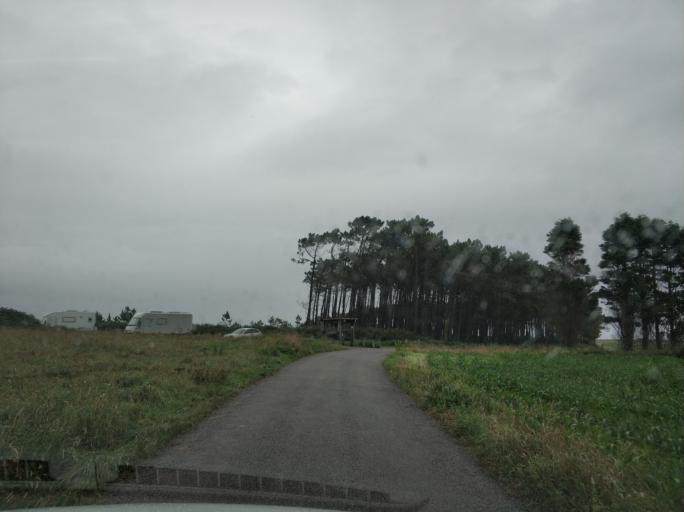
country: ES
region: Asturias
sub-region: Province of Asturias
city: Tineo
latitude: 43.5643
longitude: -6.4700
